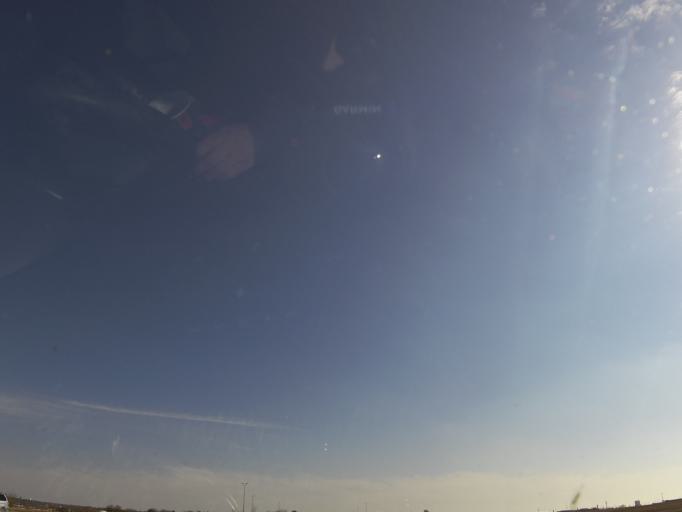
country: US
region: Minnesota
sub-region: Steele County
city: Owatonna
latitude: 44.1085
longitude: -93.2462
